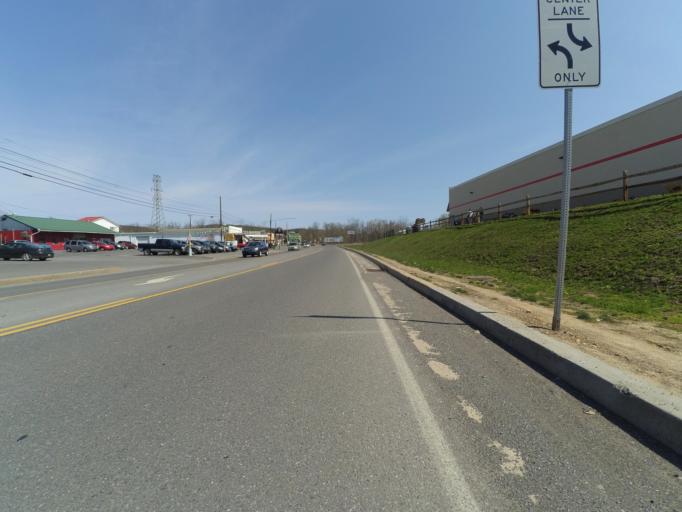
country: US
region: Pennsylvania
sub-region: Clinton County
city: Flemington
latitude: 41.1184
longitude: -77.4741
